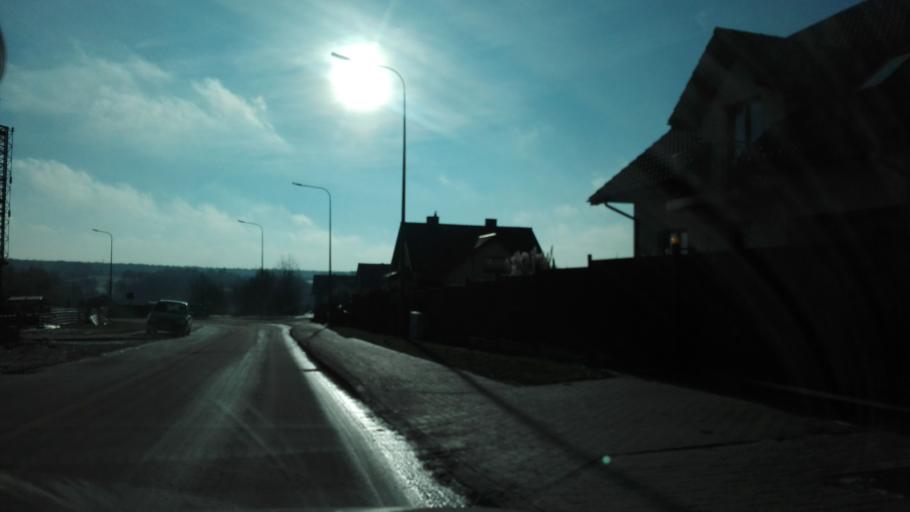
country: PL
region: Lublin Voivodeship
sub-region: Powiat lubelski
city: Kozubszczyzna
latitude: 51.2227
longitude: 22.4928
